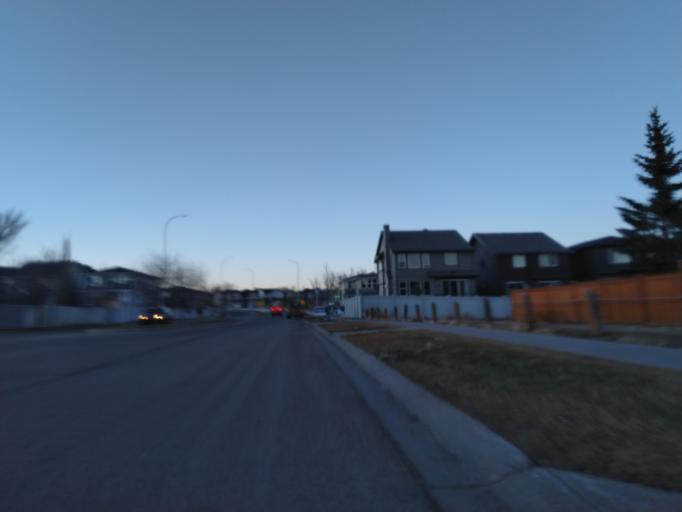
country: CA
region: Alberta
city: Calgary
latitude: 51.1307
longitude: -114.2513
